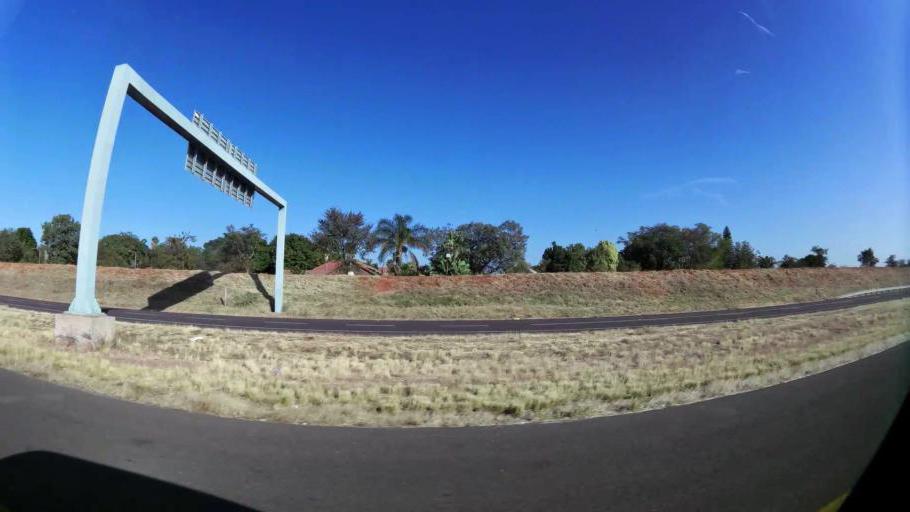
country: ZA
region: Gauteng
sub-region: City of Tshwane Metropolitan Municipality
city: Pretoria
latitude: -25.6597
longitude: 28.1143
